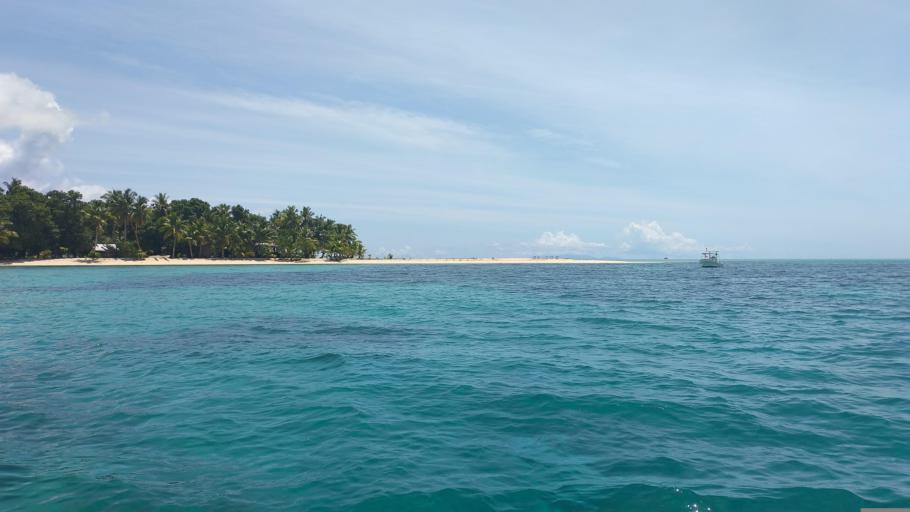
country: FJ
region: Central
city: Suva
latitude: -17.8105
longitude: 178.7206
